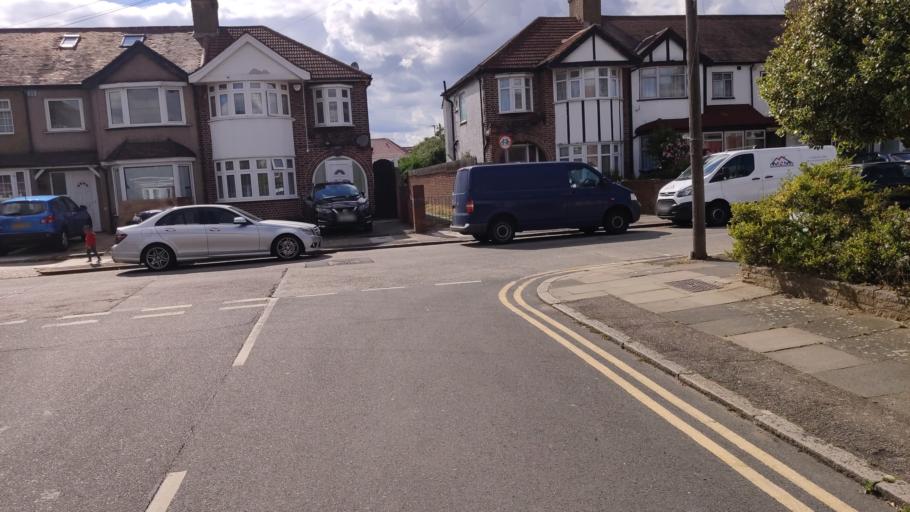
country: GB
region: England
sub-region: Greater London
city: Enfield
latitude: 51.6209
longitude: -0.0798
